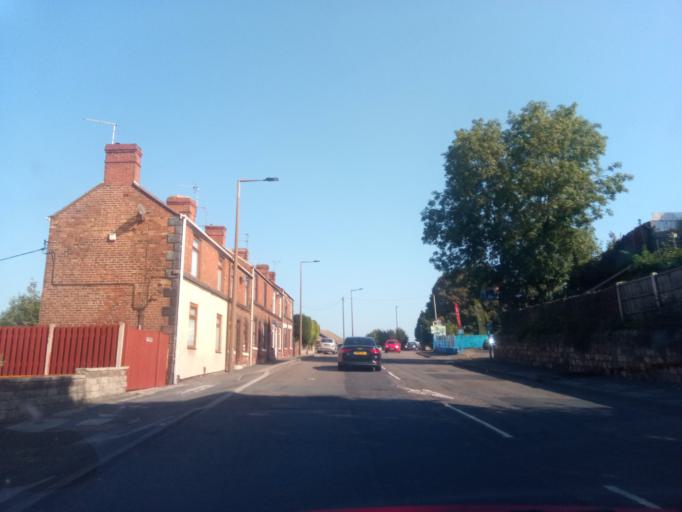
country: GB
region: England
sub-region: Doncaster
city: Conisbrough
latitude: 53.4819
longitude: -1.2245
